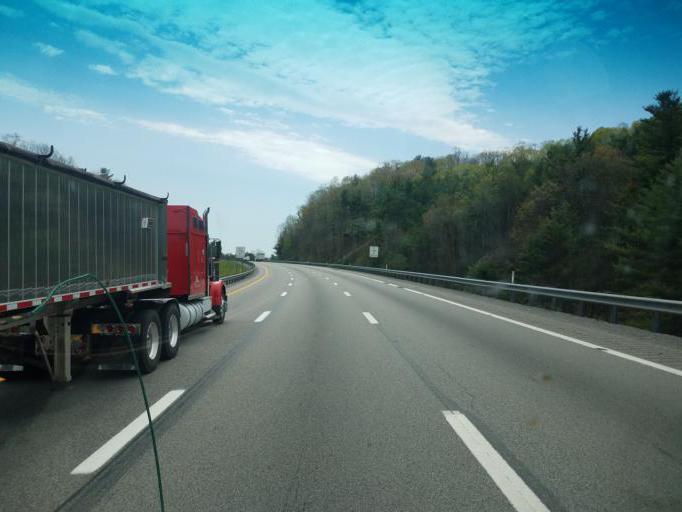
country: US
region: West Virginia
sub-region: Mercer County
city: Athens
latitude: 37.4445
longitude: -81.0666
